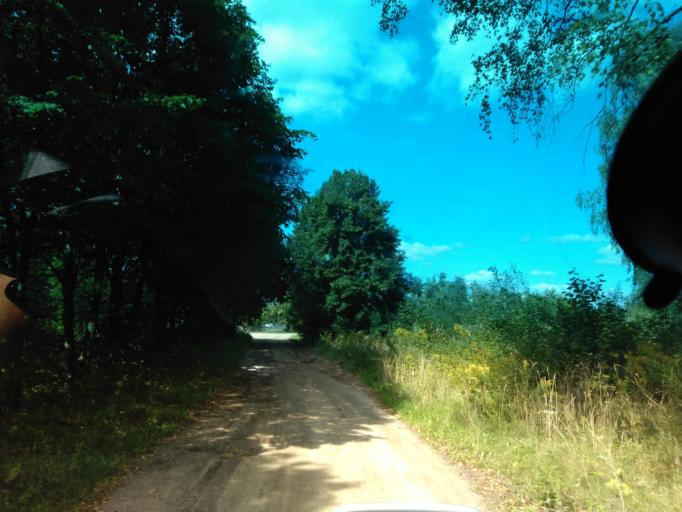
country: BY
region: Minsk
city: Stan'kava
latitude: 53.6234
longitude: 27.3156
